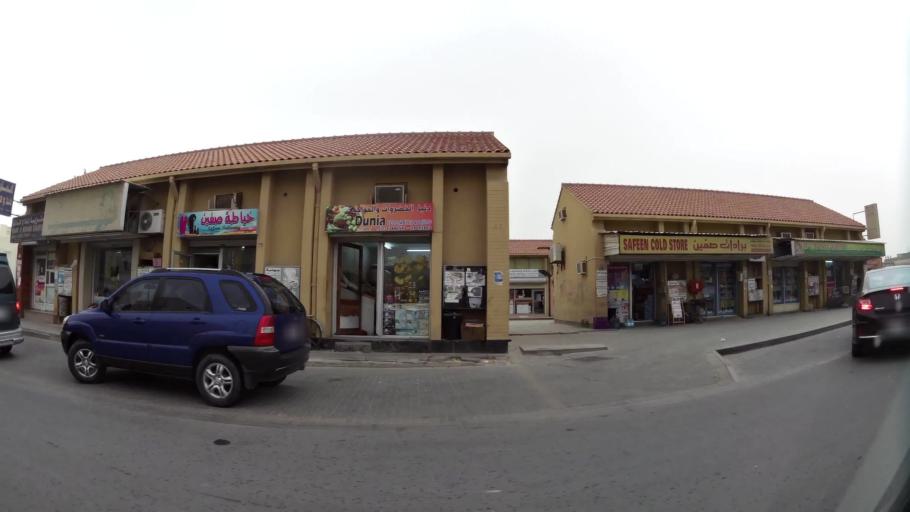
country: BH
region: Northern
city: Madinat `Isa
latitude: 26.1618
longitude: 50.5661
